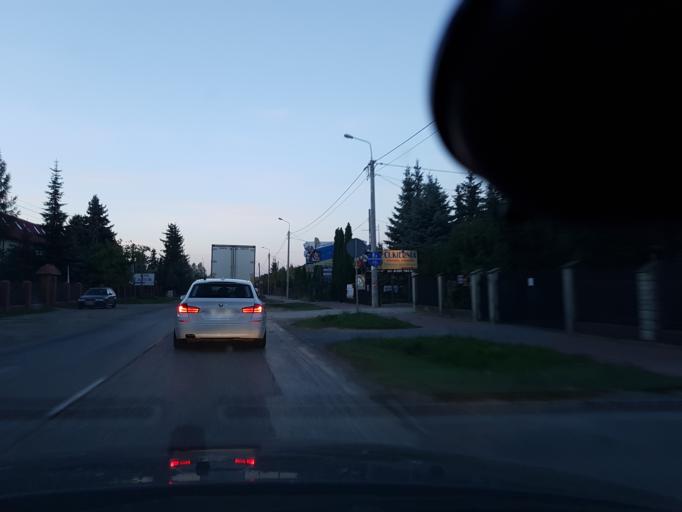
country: PL
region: Masovian Voivodeship
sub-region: Powiat grodziski
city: Grodzisk Mazowiecki
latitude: 52.0863
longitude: 20.6114
